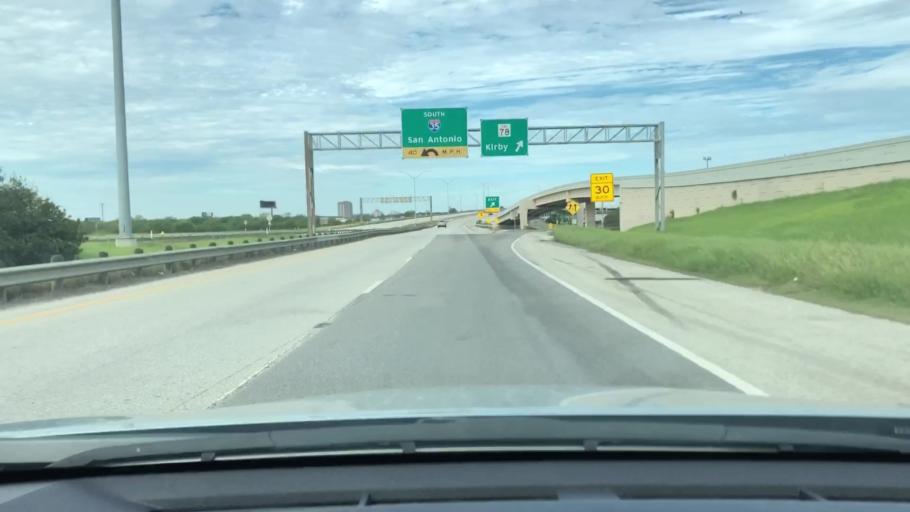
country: US
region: Texas
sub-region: Bexar County
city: Kirby
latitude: 29.4525
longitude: -98.4075
